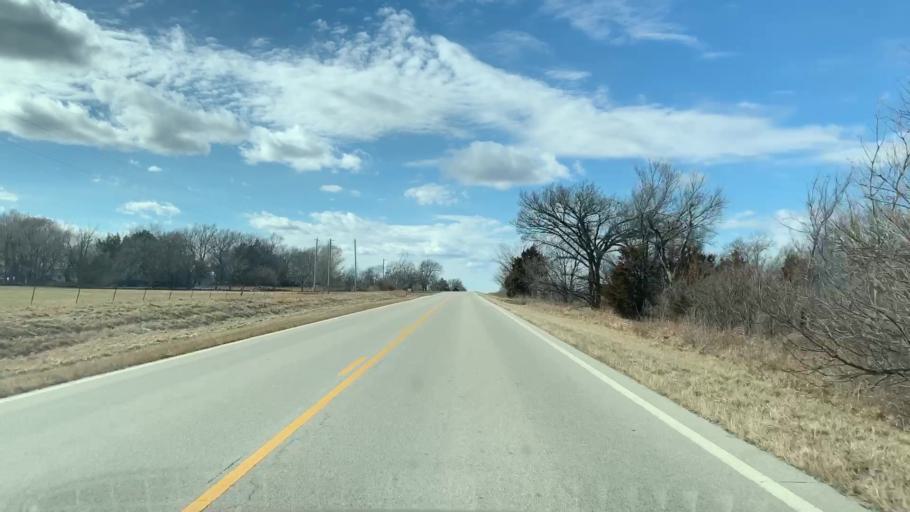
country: US
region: Kansas
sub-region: Neosho County
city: Chanute
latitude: 37.5287
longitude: -95.4415
